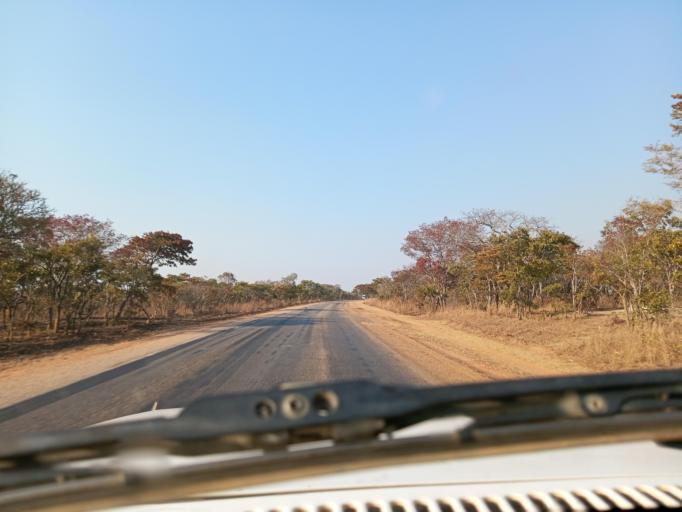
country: ZM
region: Northern
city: Mpika
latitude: -12.3673
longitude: 31.1035
